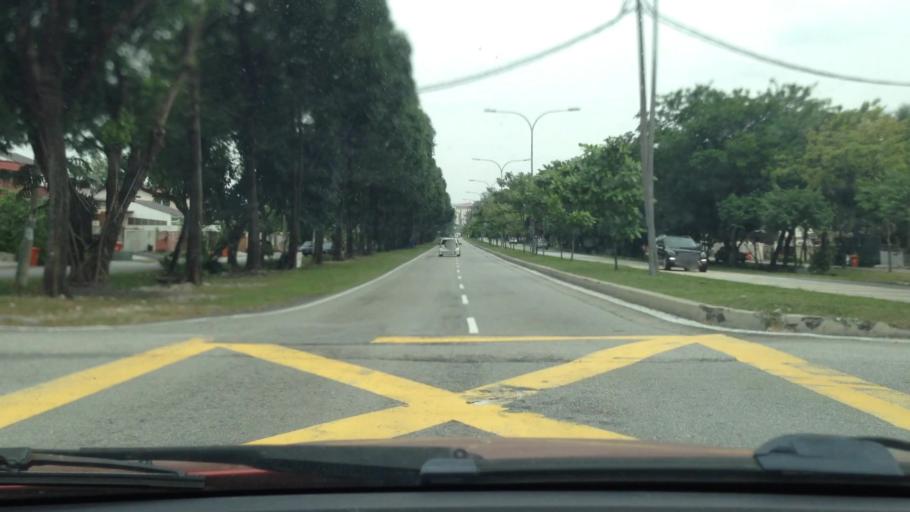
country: MY
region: Selangor
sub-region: Petaling
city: Petaling Jaya
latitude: 3.0995
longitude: 101.6072
